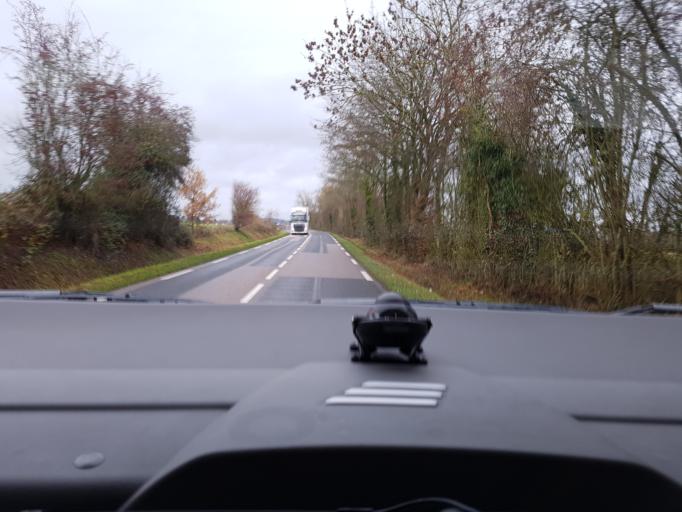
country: FR
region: Haute-Normandie
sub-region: Departement de la Seine-Maritime
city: Gournay-en-Bray
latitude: 49.4699
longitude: 1.7075
